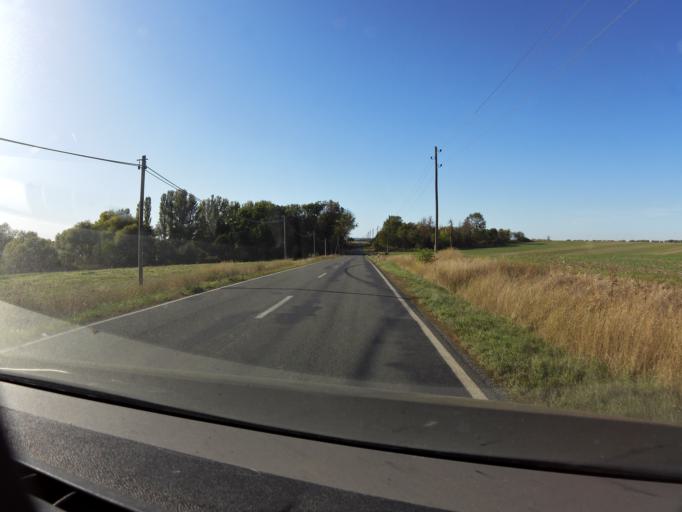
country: DE
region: Saxony-Anhalt
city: Wegeleben
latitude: 51.8804
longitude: 11.2135
